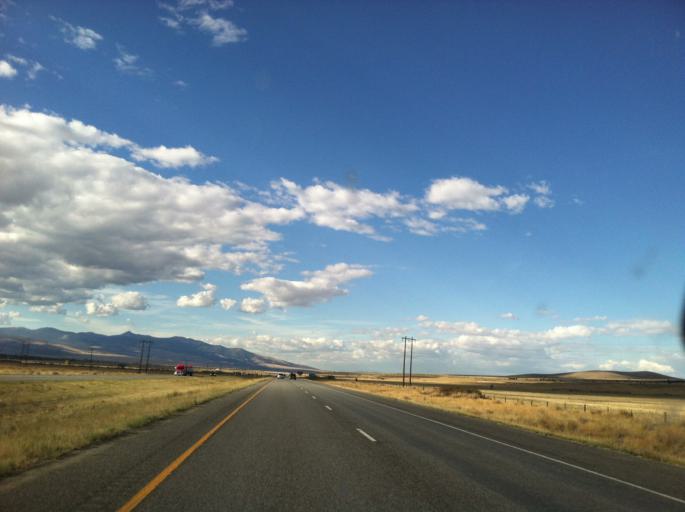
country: US
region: Montana
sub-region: Deer Lodge County
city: Warm Springs
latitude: 46.0787
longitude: -112.7868
